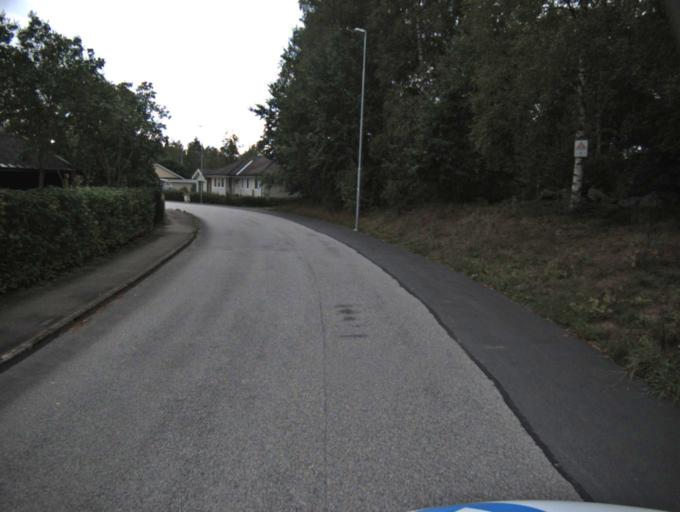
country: SE
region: Vaestra Goetaland
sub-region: Boras Kommun
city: Dalsjofors
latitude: 57.8283
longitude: 13.1871
